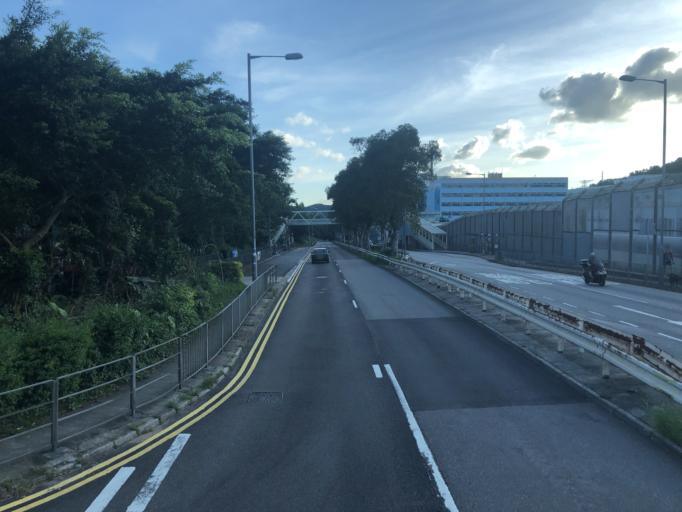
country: HK
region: Sai Kung
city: Sai Kung
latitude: 22.3402
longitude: 114.2473
